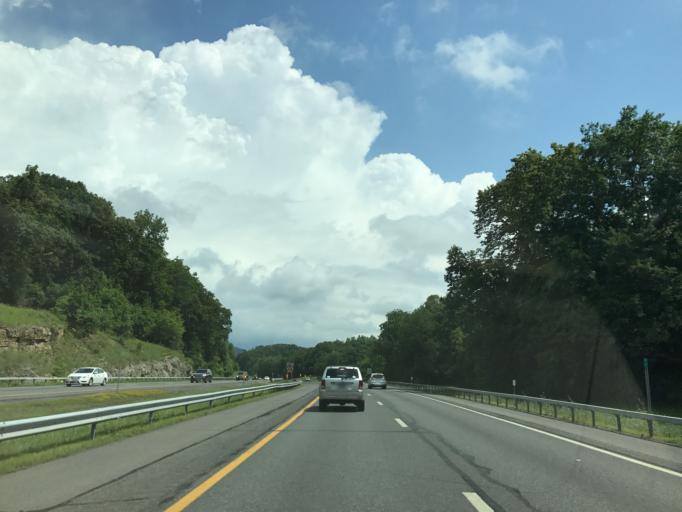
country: US
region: New York
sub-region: Greene County
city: Coxsackie
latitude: 42.3668
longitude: -73.8455
